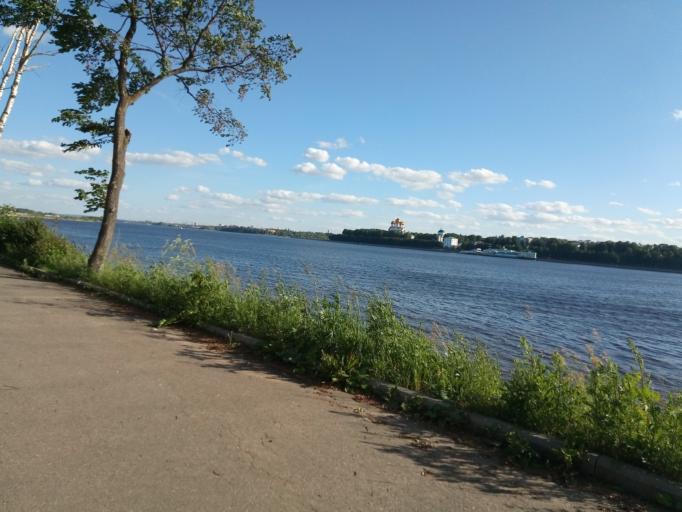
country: RU
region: Jaroslavl
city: Yaroslavl
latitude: 57.6329
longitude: 39.9069
